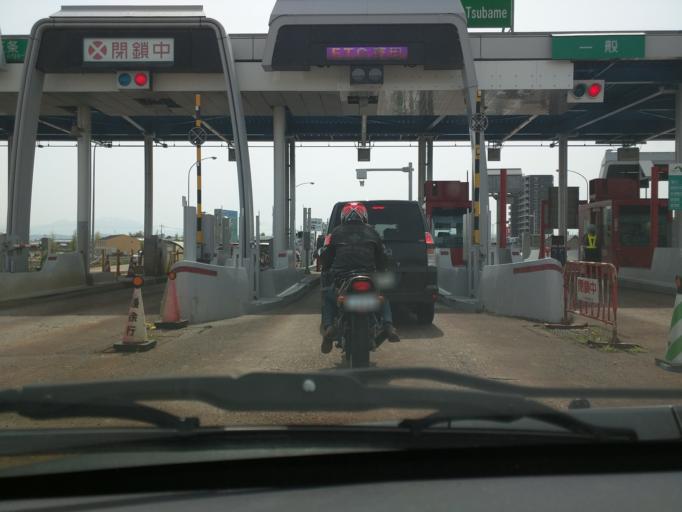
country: JP
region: Niigata
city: Tsubame
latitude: 37.6515
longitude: 138.9418
